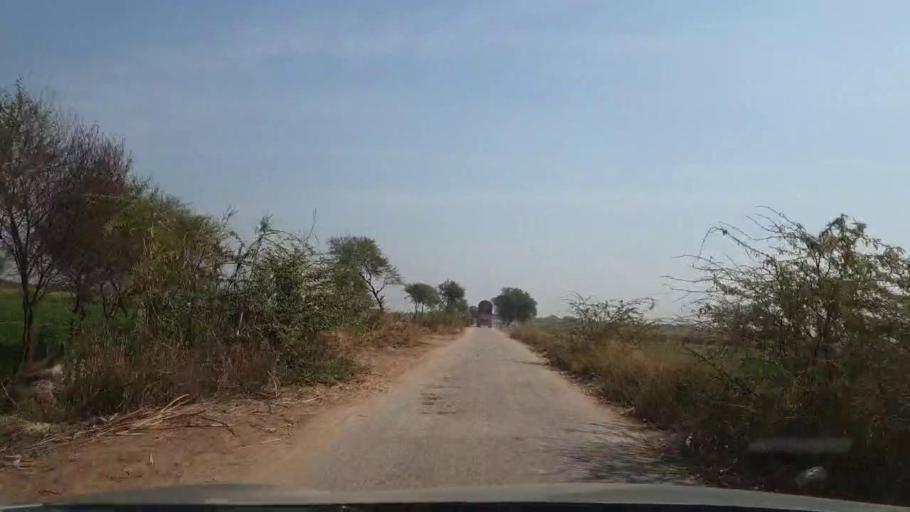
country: PK
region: Sindh
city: Tando Adam
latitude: 25.6283
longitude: 68.7290
